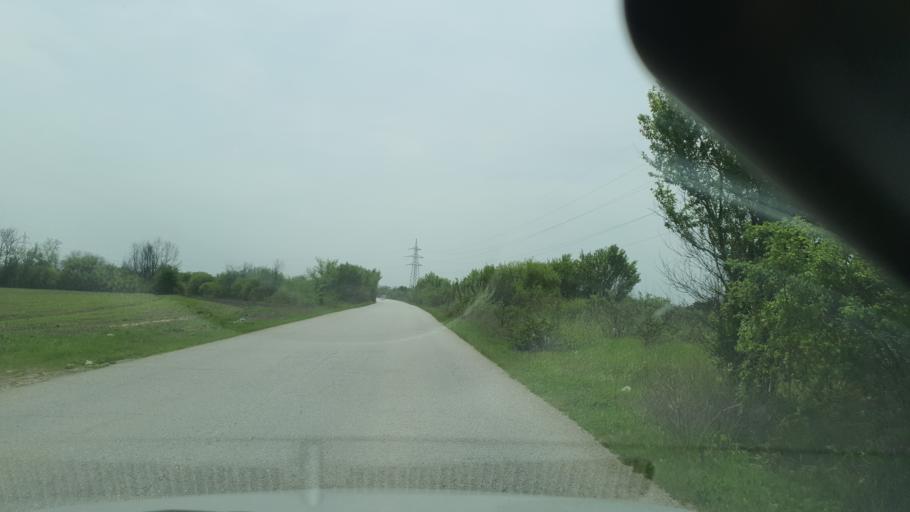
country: RS
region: Central Serbia
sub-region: Branicevski Okrug
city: Pozarevac
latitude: 44.6761
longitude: 21.1623
